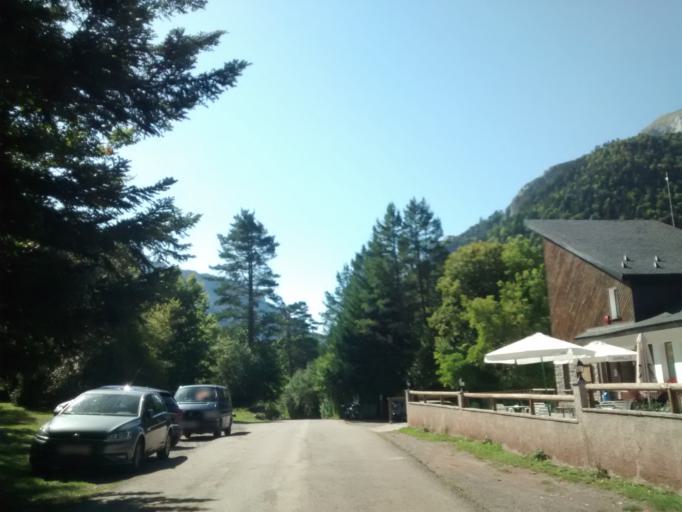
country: ES
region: Aragon
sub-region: Provincia de Huesca
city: Aragues del Puerto
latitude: 42.8347
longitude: -0.7112
